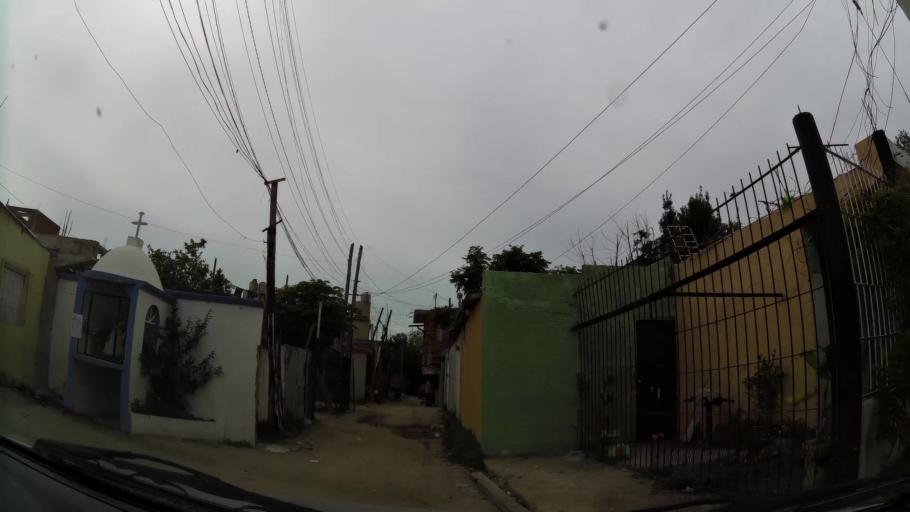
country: AR
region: Buenos Aires
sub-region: Partido de Avellaneda
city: Avellaneda
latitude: -34.6464
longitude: -58.3520
